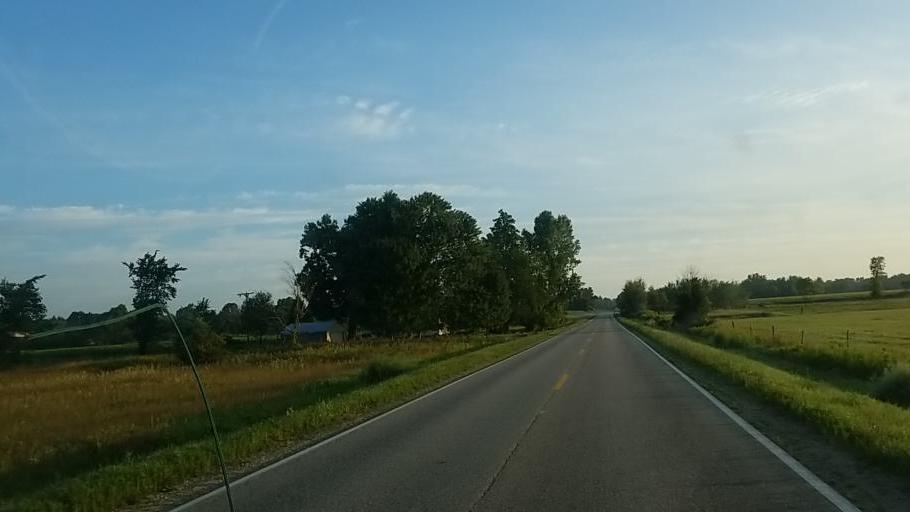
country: US
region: Michigan
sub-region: Montcalm County
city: Howard City
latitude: 43.3418
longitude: -85.4031
